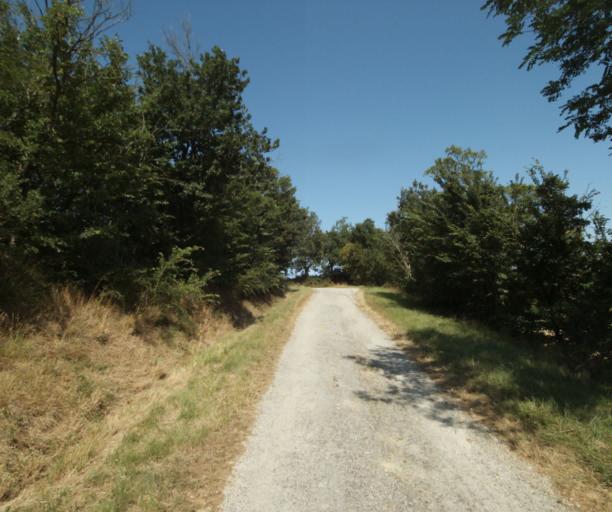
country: FR
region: Midi-Pyrenees
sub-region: Departement de la Haute-Garonne
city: Saint-Felix-Lauragais
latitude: 43.4389
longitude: 1.8507
